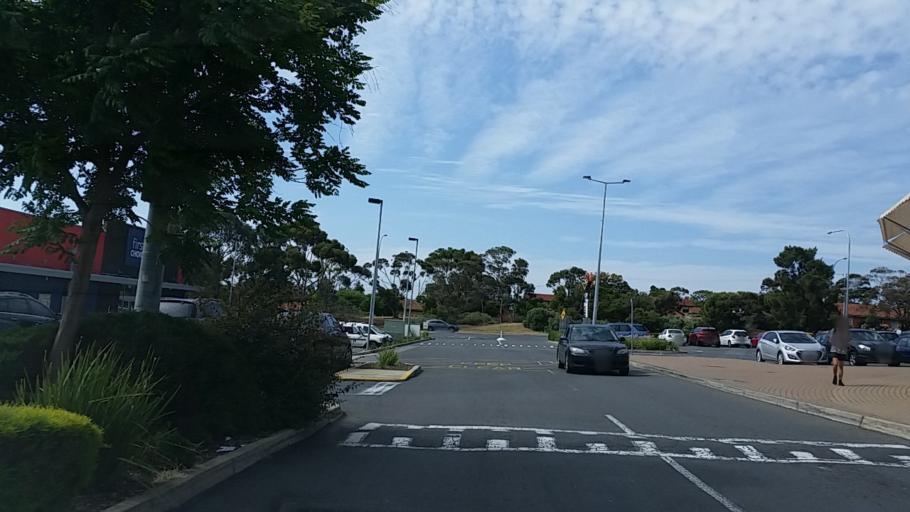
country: AU
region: South Australia
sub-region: Salisbury
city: Ingle Farm
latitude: -34.8287
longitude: 138.6480
